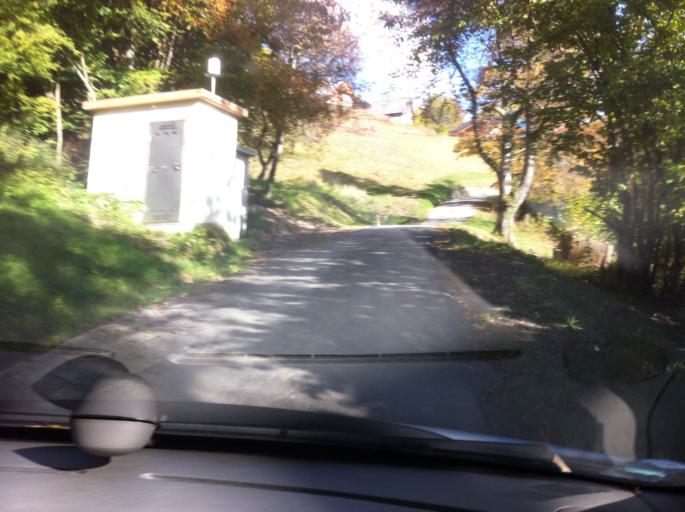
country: FR
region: Rhone-Alpes
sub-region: Departement de la Haute-Savoie
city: Faverges
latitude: 45.7772
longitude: 6.3052
